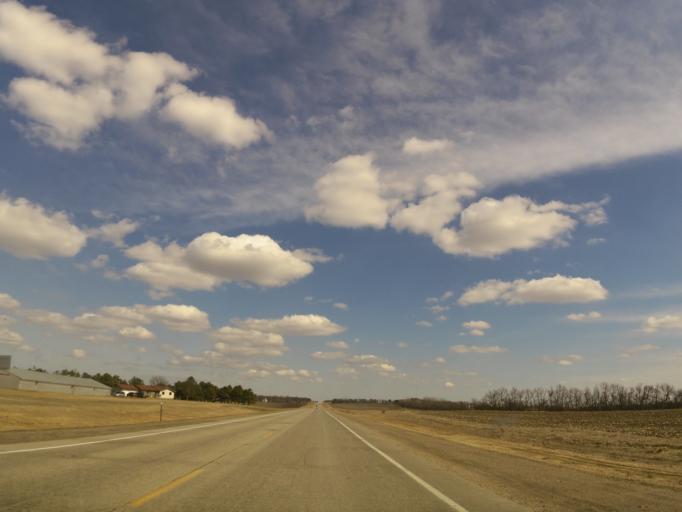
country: US
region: South Dakota
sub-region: Codington County
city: Watertown
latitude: 44.8899
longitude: -96.9126
